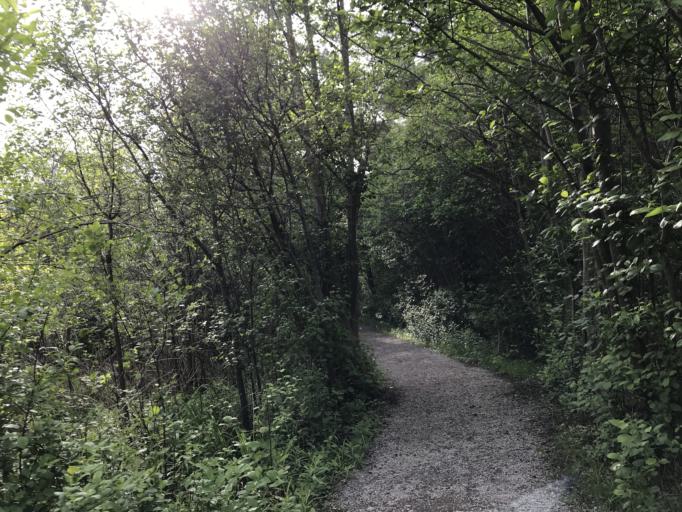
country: US
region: Michigan
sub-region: Oakland County
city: Farmington
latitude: 42.4736
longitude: -83.3810
